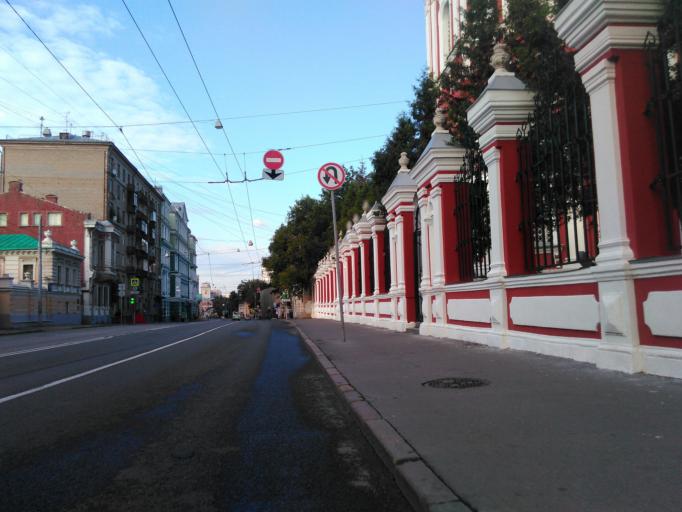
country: RU
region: Moscow
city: Taganskiy
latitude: 55.7656
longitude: 37.6615
